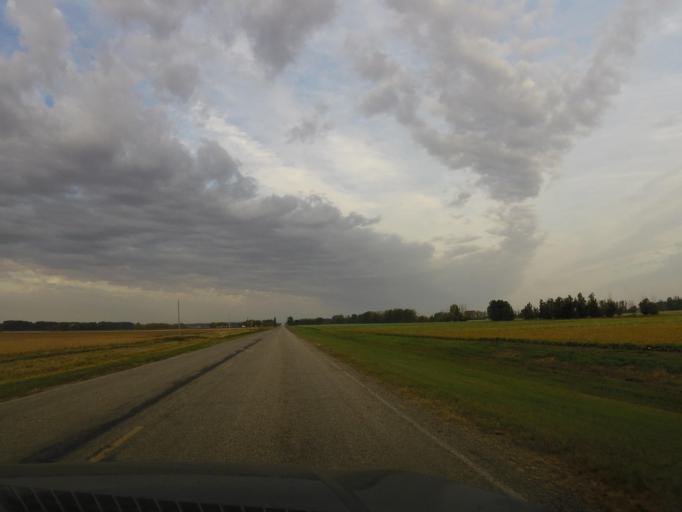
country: US
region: North Dakota
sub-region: Pembina County
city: Cavalier
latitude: 48.6882
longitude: -97.6272
